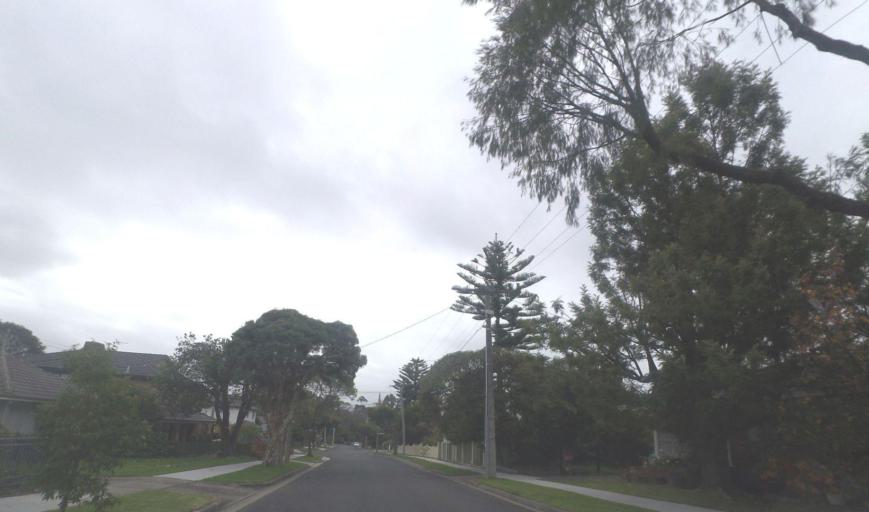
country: AU
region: Victoria
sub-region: Whitehorse
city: Blackburn North
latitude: -37.8034
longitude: 145.1573
